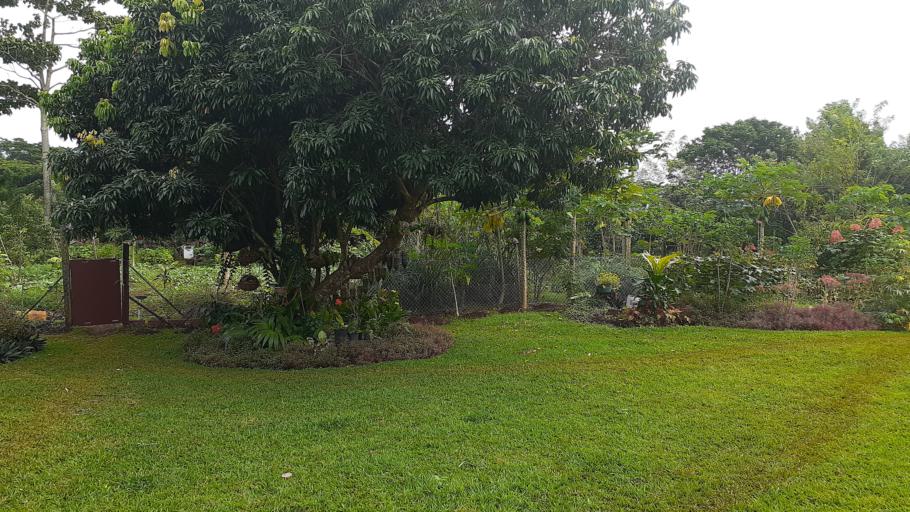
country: VU
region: Shefa
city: Port-Vila
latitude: -17.7233
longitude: 168.3412
